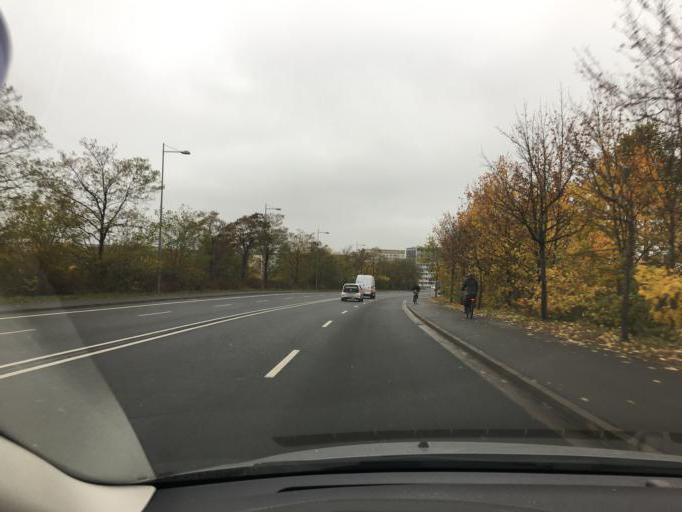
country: DE
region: Saxony
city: Leipzig
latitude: 51.3205
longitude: 12.3126
